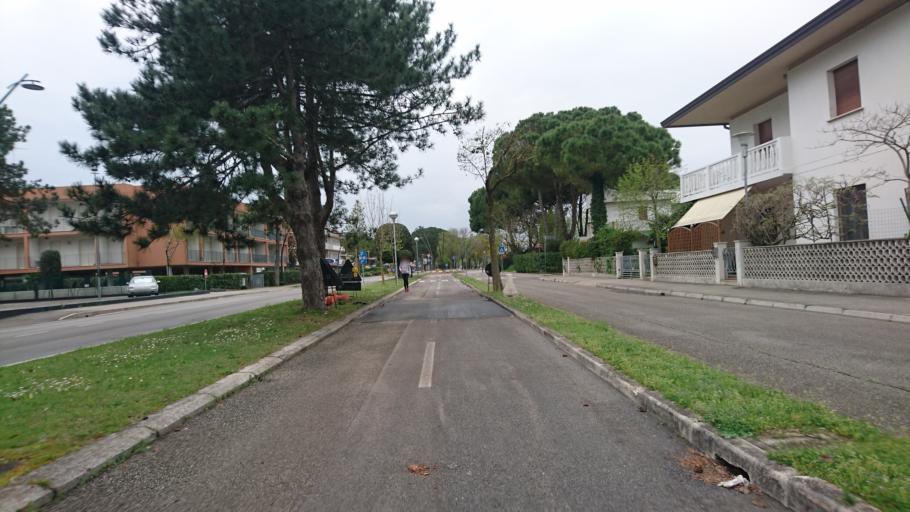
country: IT
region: Veneto
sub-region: Provincia di Venezia
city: Bibione
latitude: 45.6384
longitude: 13.0560
